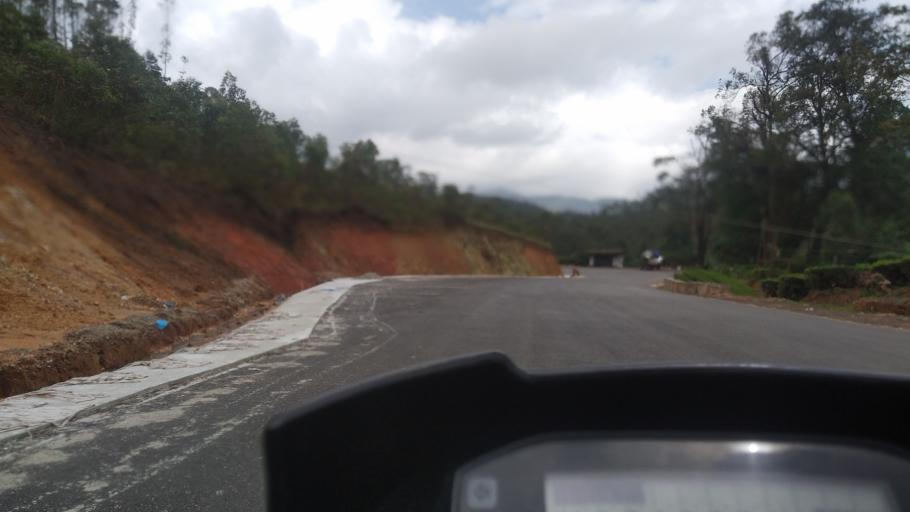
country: IN
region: Kerala
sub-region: Idukki
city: Munnar
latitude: 10.0727
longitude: 77.0918
